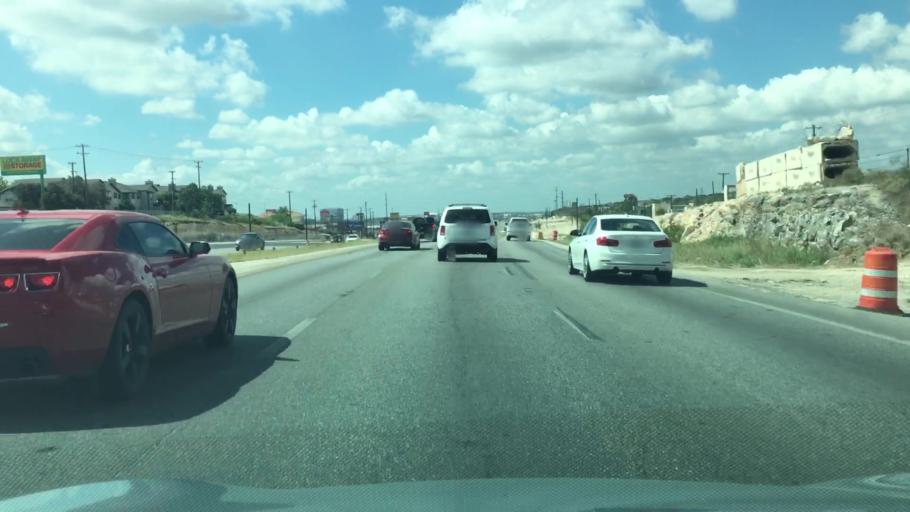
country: US
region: Texas
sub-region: Bexar County
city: Hollywood Park
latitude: 29.6446
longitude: -98.4531
